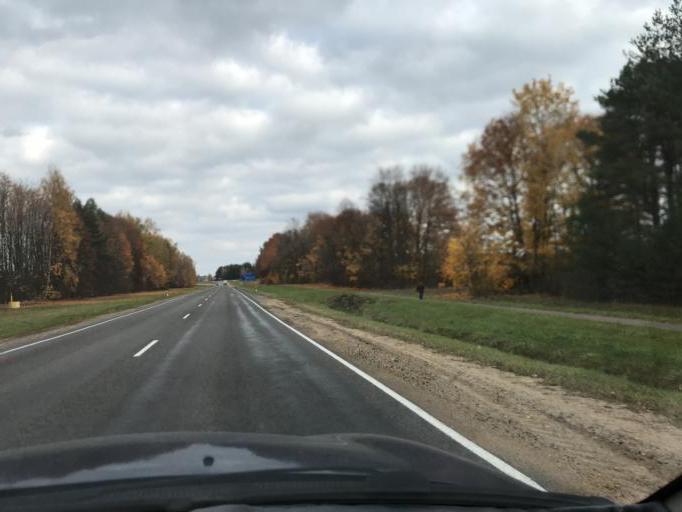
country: BY
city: Berezovka
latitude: 53.7537
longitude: 25.3859
